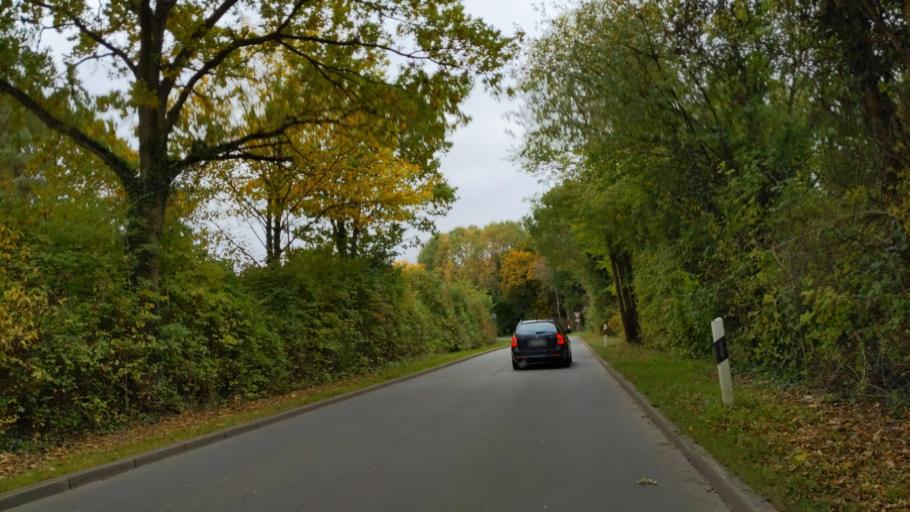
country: DE
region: Schleswig-Holstein
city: Scharbeutz
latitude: 54.0361
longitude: 10.7238
